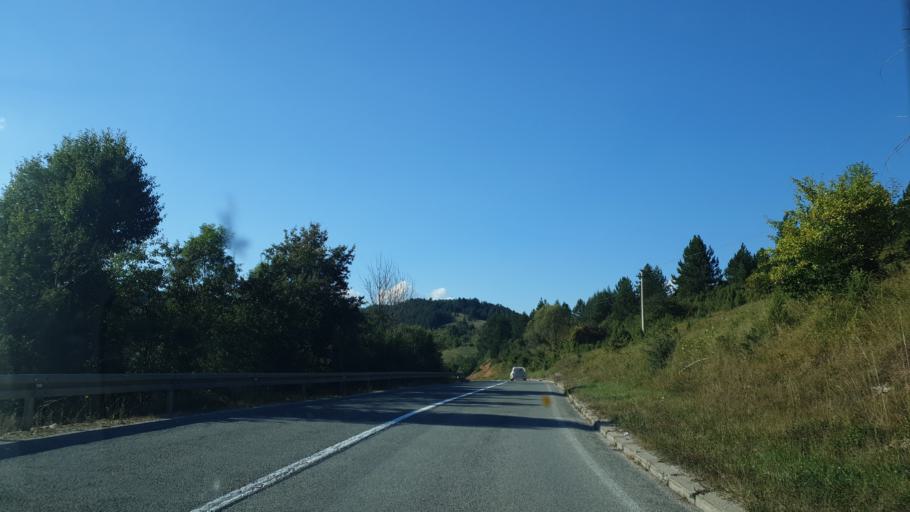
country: RS
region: Central Serbia
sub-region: Zlatiborski Okrug
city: Nova Varos
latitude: 43.5465
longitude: 19.7830
